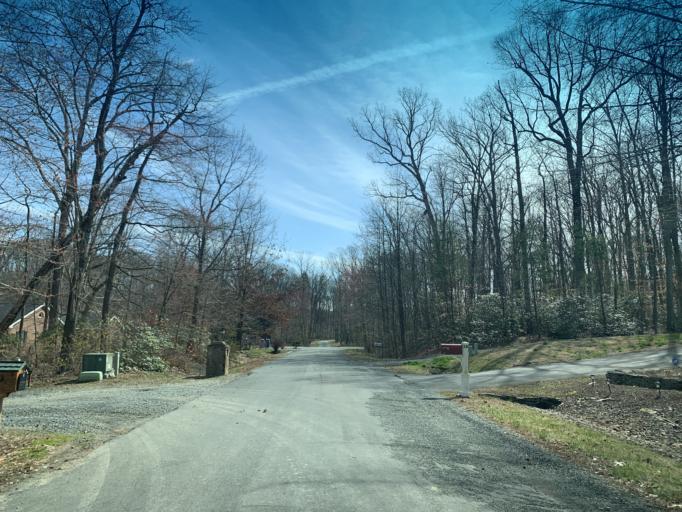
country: US
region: Maryland
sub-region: Cecil County
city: Charlestown
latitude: 39.5579
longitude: -76.0106
